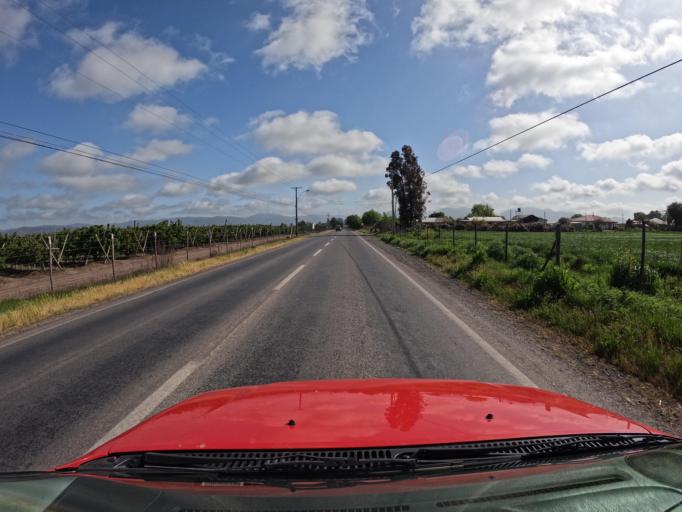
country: CL
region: Maule
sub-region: Provincia de Curico
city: Rauco
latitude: -34.8970
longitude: -71.2736
